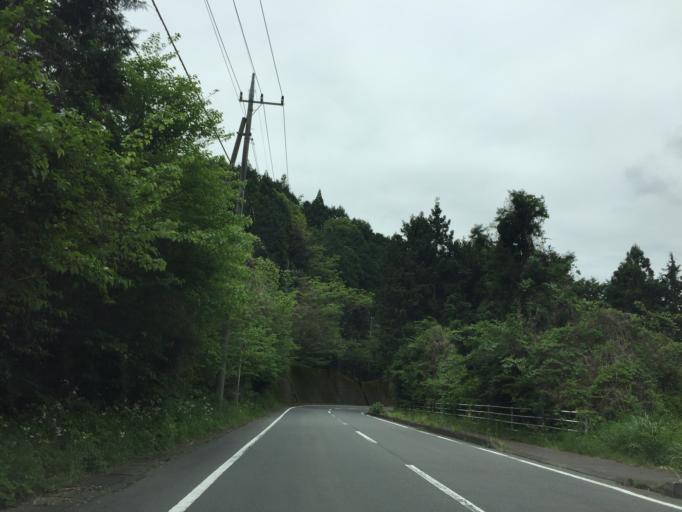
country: JP
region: Shizuoka
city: Gotemba
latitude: 35.2204
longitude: 138.9352
